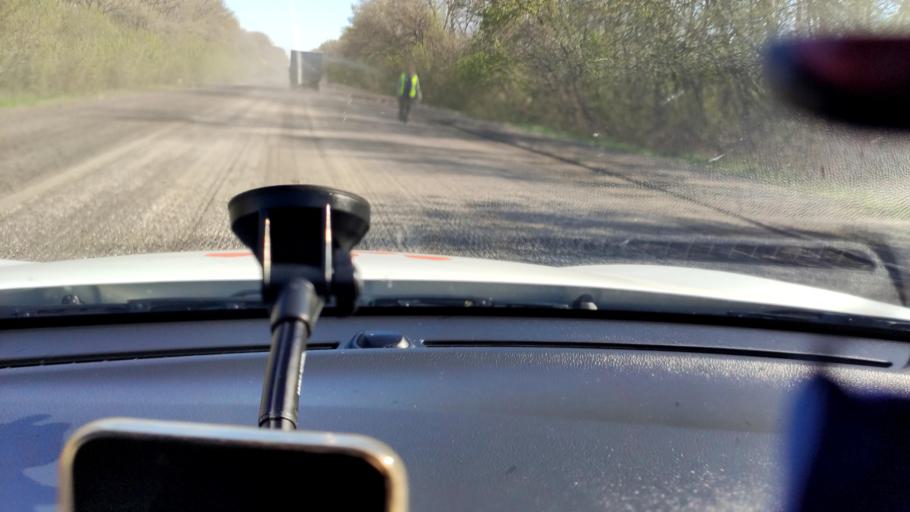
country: RU
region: Voronezj
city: Uryv-Pokrovka
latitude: 51.2225
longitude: 39.0641
